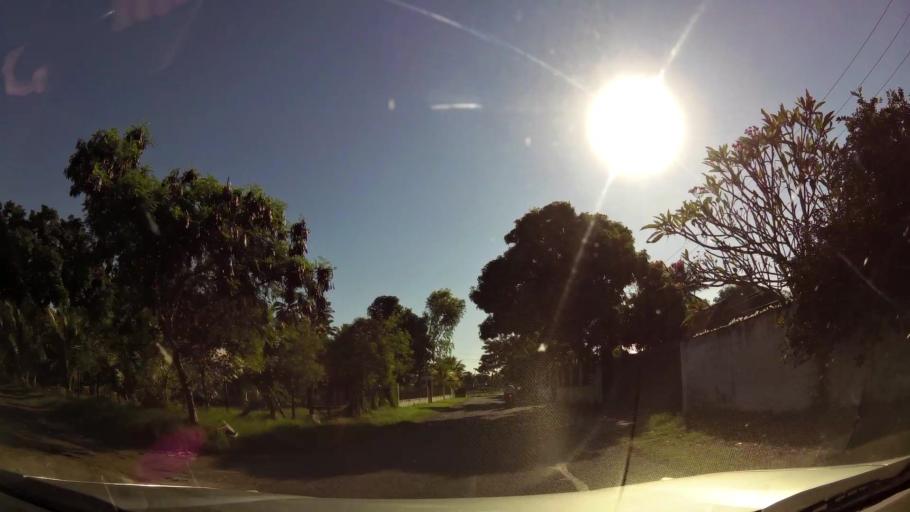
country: GT
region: Santa Rosa
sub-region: Municipio de Taxisco
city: Taxisco
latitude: 13.8960
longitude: -90.4861
